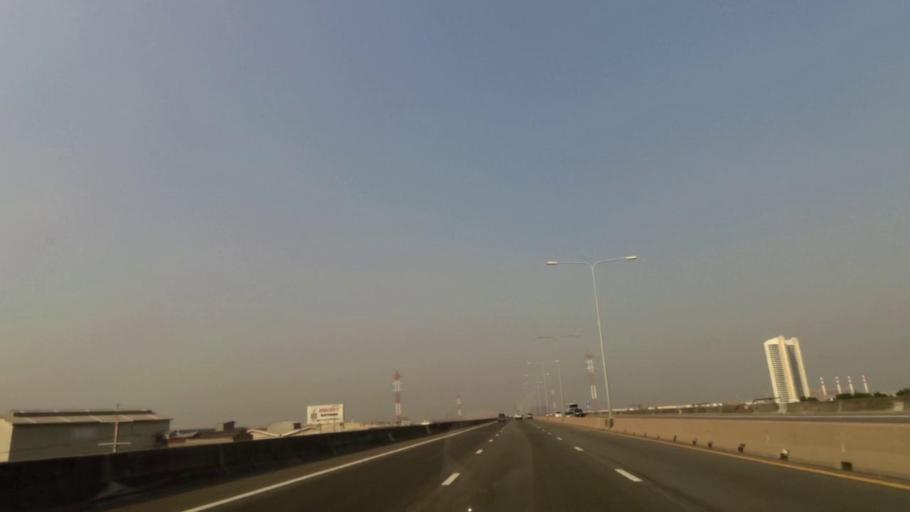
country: TH
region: Chachoengsao
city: Bang Pakong
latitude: 13.4827
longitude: 101.0015
